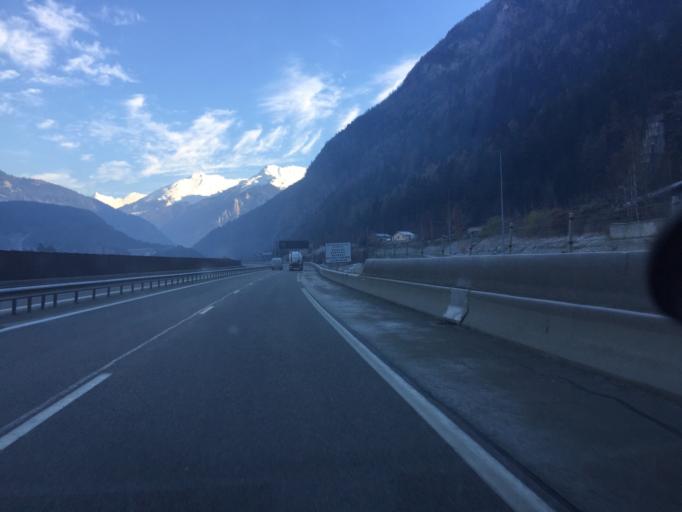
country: FR
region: Rhone-Alpes
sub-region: Departement de la Savoie
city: Modane
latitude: 45.2028
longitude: 6.5866
